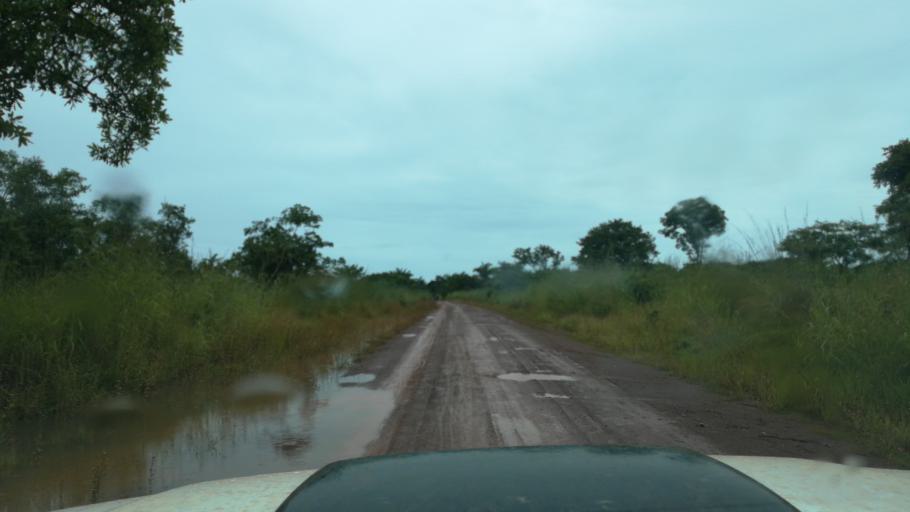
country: ZM
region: Luapula
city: Mwense
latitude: -10.1457
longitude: 28.1231
